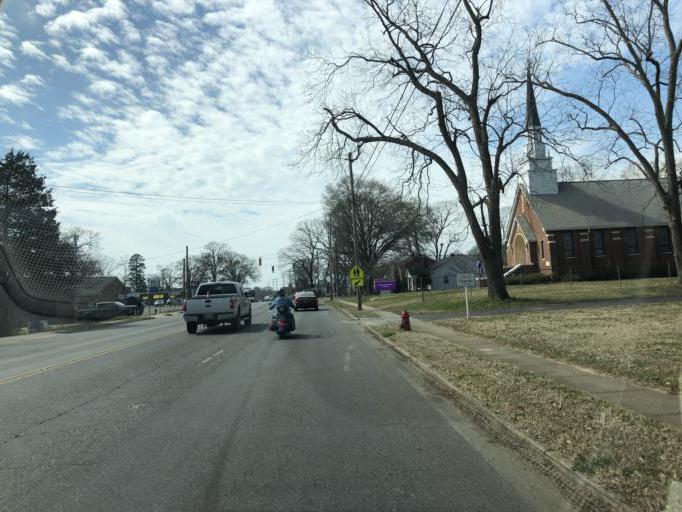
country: US
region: North Carolina
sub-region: Gaston County
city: Dallas
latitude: 35.3168
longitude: -81.1808
